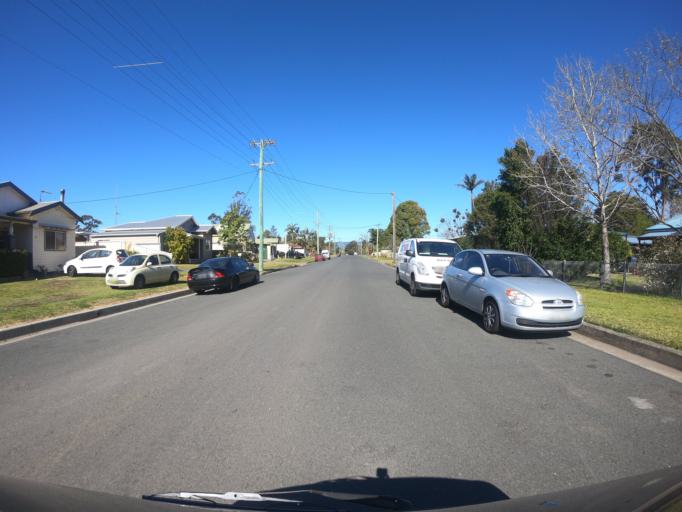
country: AU
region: New South Wales
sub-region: Wollongong
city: Dapto
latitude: -34.4904
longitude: 150.7923
